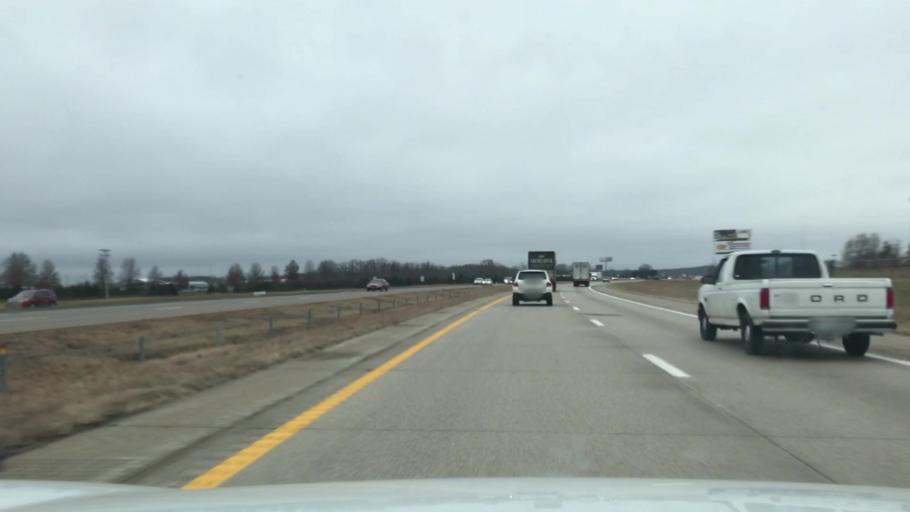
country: US
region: Missouri
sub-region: Franklin County
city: Sullivan
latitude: 38.2008
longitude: -91.1796
